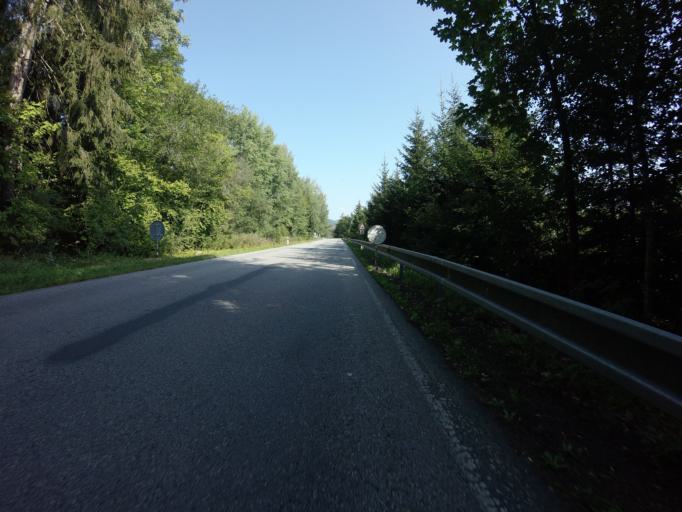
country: CZ
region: Jihocesky
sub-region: Okres Cesky Krumlov
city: Vyssi Brod
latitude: 48.5956
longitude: 14.3226
